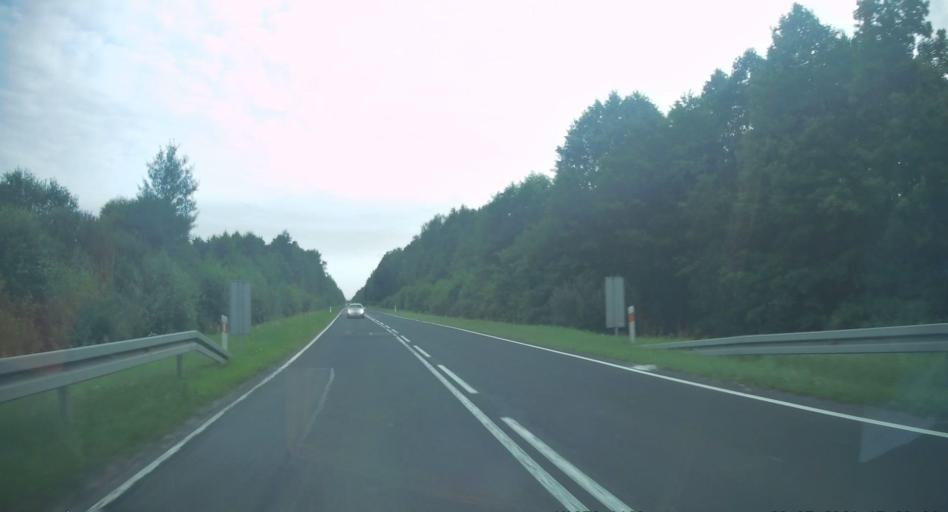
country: PL
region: Lodz Voivodeship
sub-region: Powiat radomszczanski
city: Plawno
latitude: 51.0151
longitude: 19.4224
